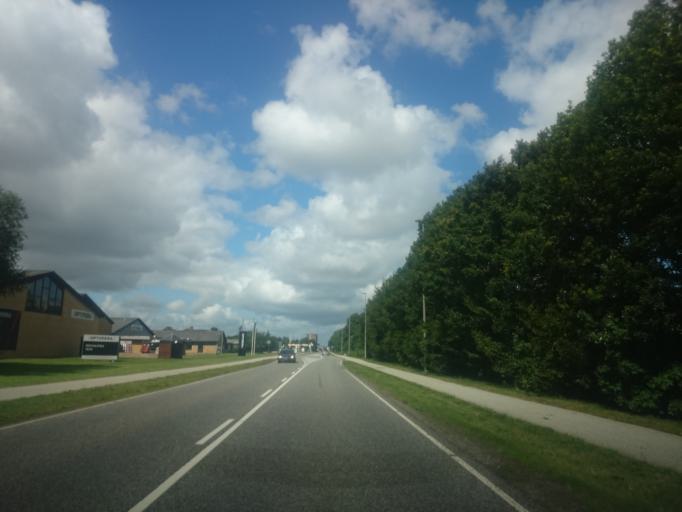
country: DK
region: South Denmark
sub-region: Billund Kommune
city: Billund
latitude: 55.7264
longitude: 9.1265
